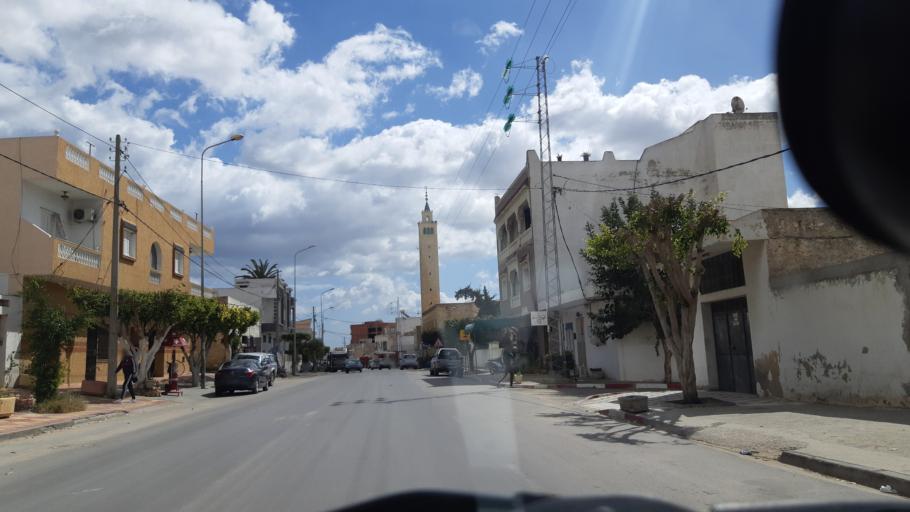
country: TN
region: Susah
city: Akouda
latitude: 35.8741
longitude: 10.5448
